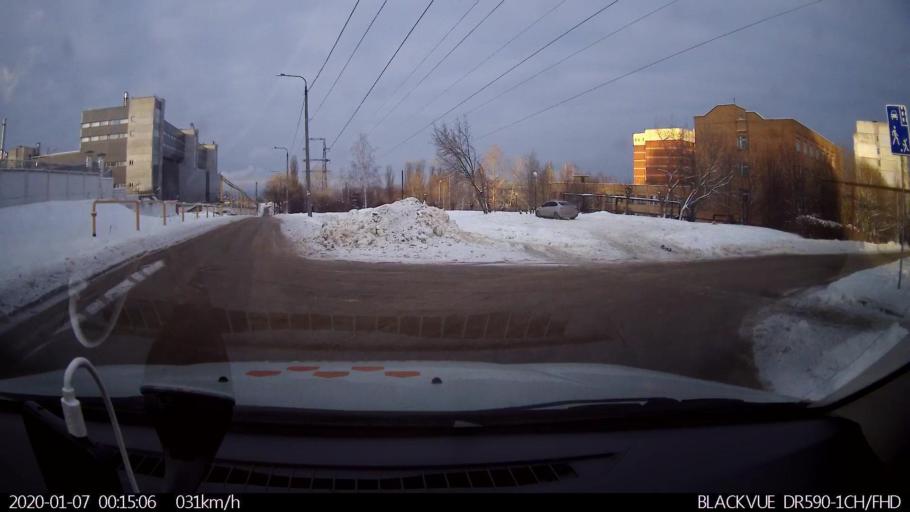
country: RU
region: Nizjnij Novgorod
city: Nizhniy Novgorod
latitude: 56.2338
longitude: 43.9431
